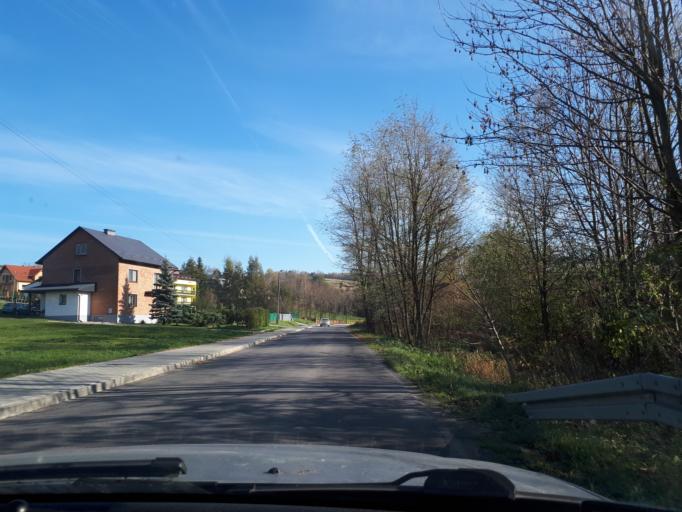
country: PL
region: Subcarpathian Voivodeship
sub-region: Powiat debicki
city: Debica
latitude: 50.0040
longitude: 21.4039
